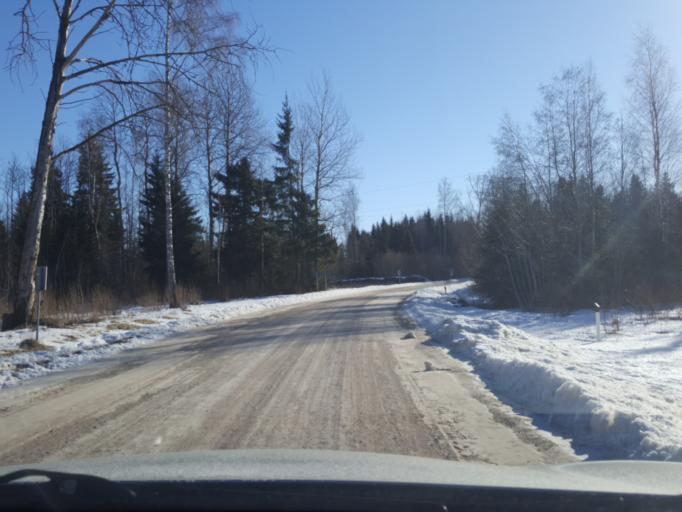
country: EE
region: Viljandimaa
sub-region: Suure-Jaani vald
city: Suure-Jaani
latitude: 58.4646
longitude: 25.5460
